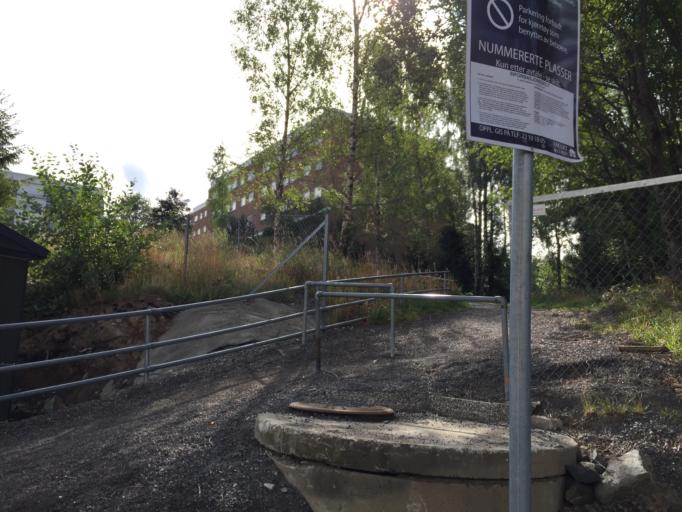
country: NO
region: Akershus
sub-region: Skedsmo
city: Lillestrom
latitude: 59.9305
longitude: 11.0346
